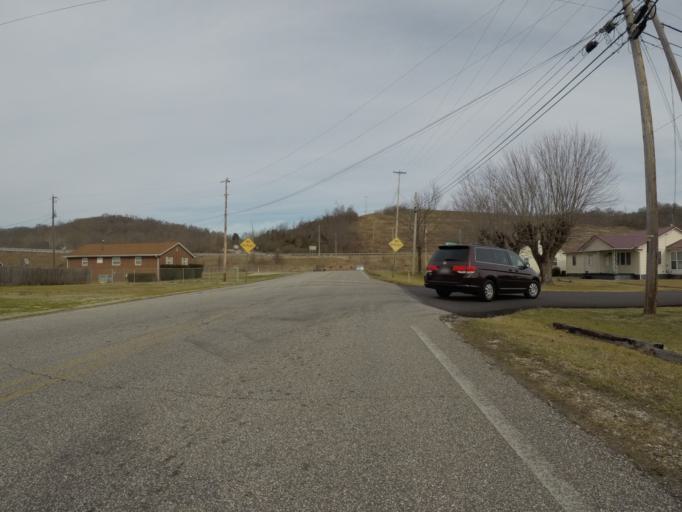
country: US
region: West Virginia
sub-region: Cabell County
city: Pea Ridge
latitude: 38.4471
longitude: -82.3761
